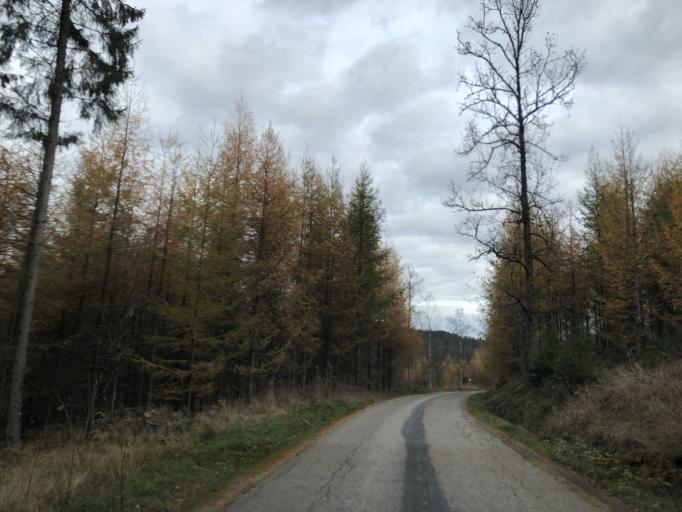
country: SE
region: Vaestra Goetaland
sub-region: Ulricehamns Kommun
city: Ulricehamn
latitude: 57.7273
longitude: 13.3625
